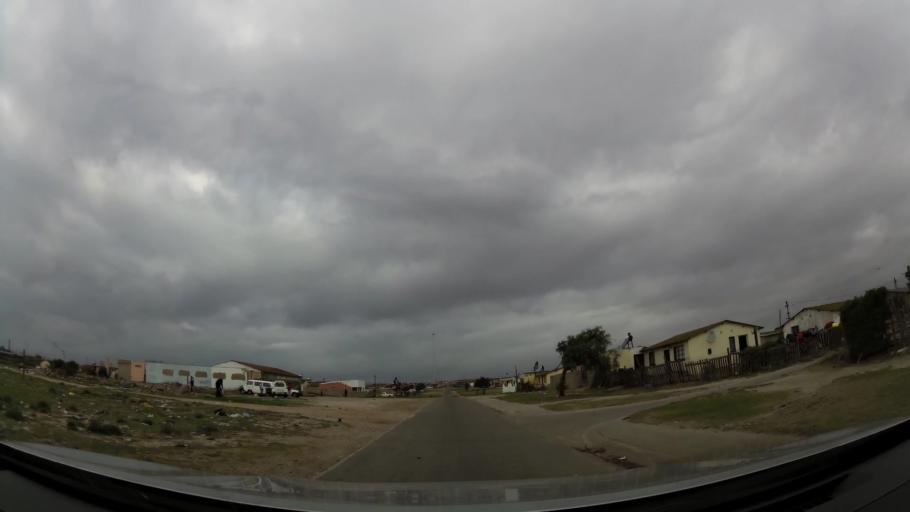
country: ZA
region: Eastern Cape
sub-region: Nelson Mandela Bay Metropolitan Municipality
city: Port Elizabeth
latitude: -33.8813
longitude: 25.6024
